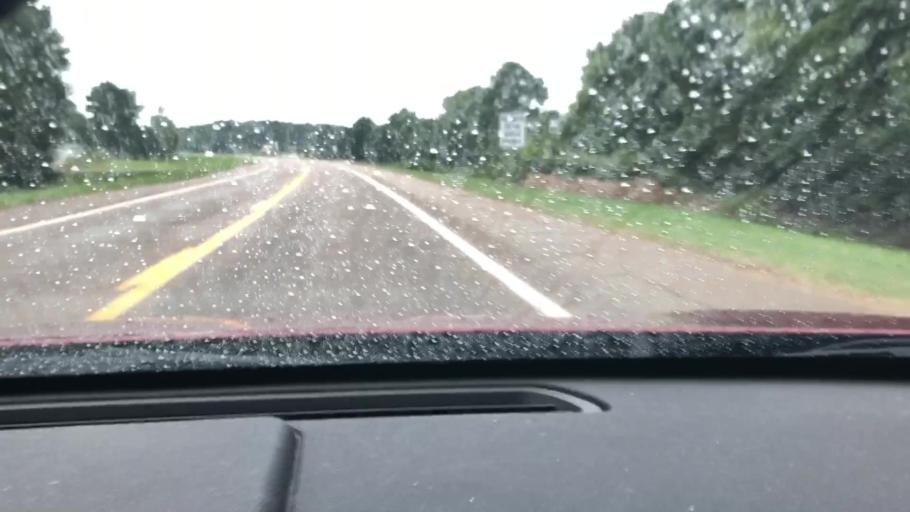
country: US
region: Arkansas
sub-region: Columbia County
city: Magnolia
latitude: 33.2966
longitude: -93.2572
